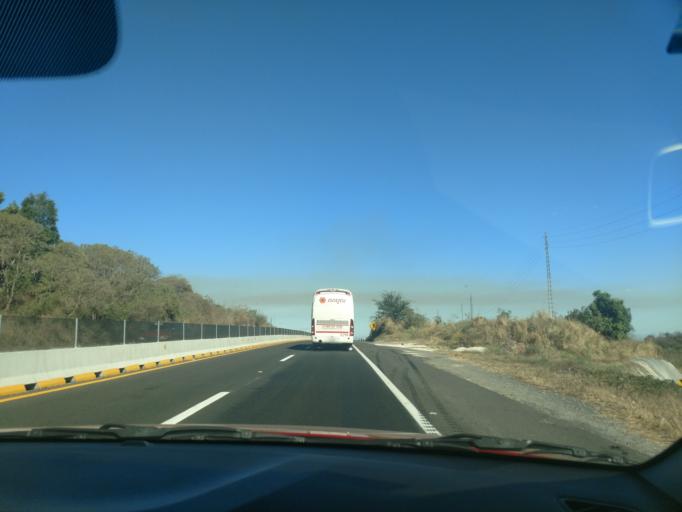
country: MX
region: Nayarit
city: Tepic
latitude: 21.5598
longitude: -104.9675
